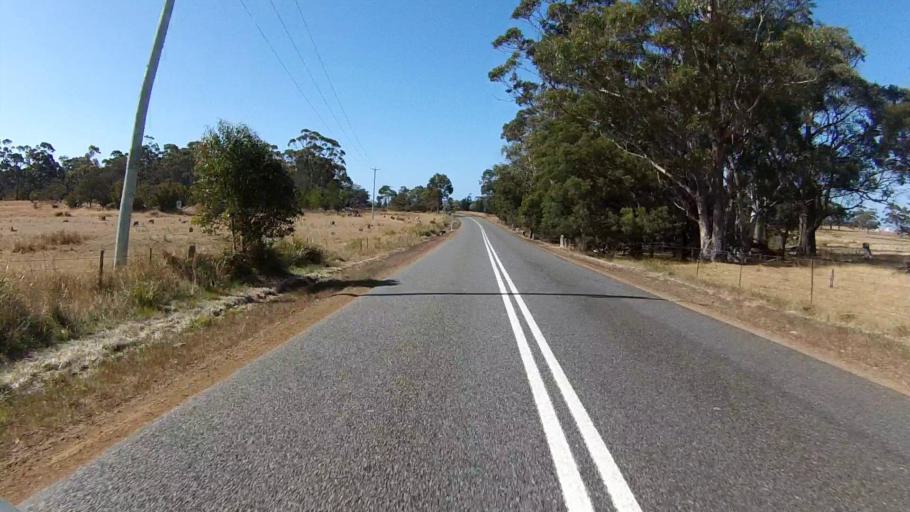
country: AU
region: Tasmania
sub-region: Sorell
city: Sorell
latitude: -42.2895
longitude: 147.9936
